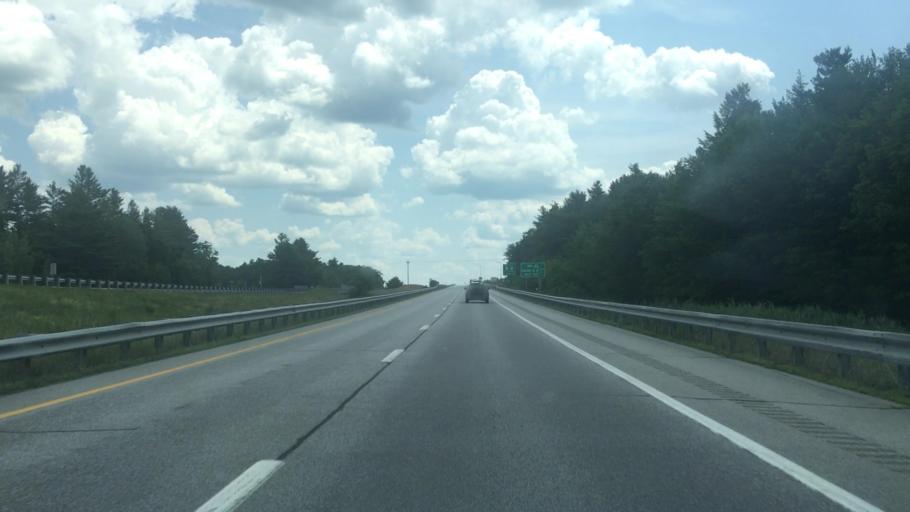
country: US
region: New Hampshire
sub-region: Merrimack County
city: New London
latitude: 43.4299
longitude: -72.0409
